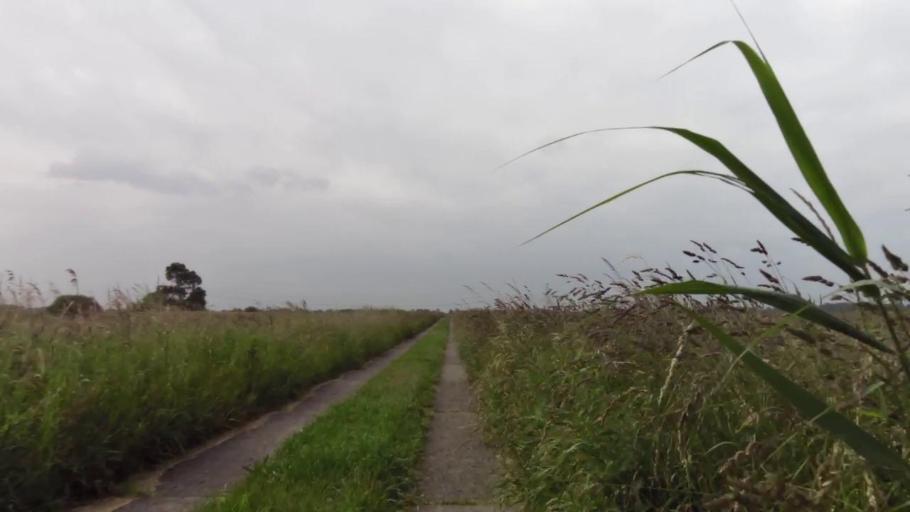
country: PL
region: West Pomeranian Voivodeship
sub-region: Powiat goleniowski
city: Stepnica
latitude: 53.5672
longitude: 14.6969
